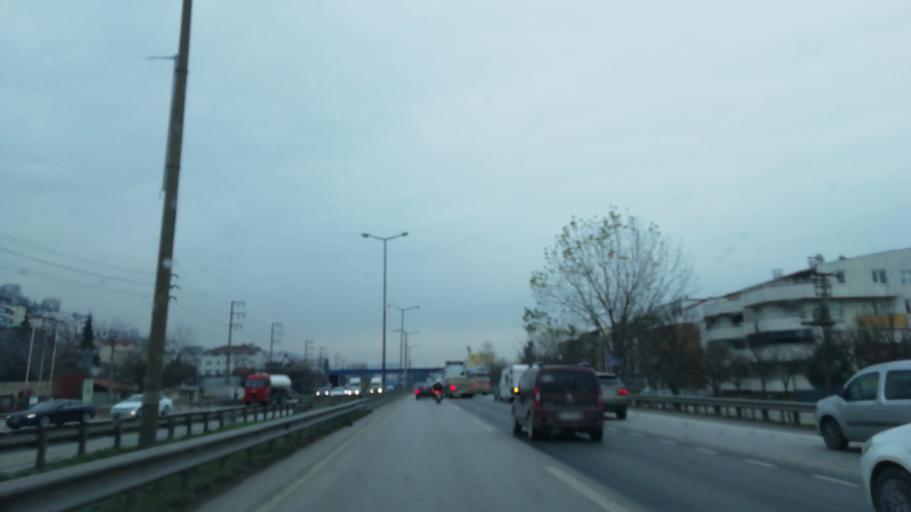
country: TR
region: Kocaeli
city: Izmit
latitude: 40.7630
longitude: 29.8823
